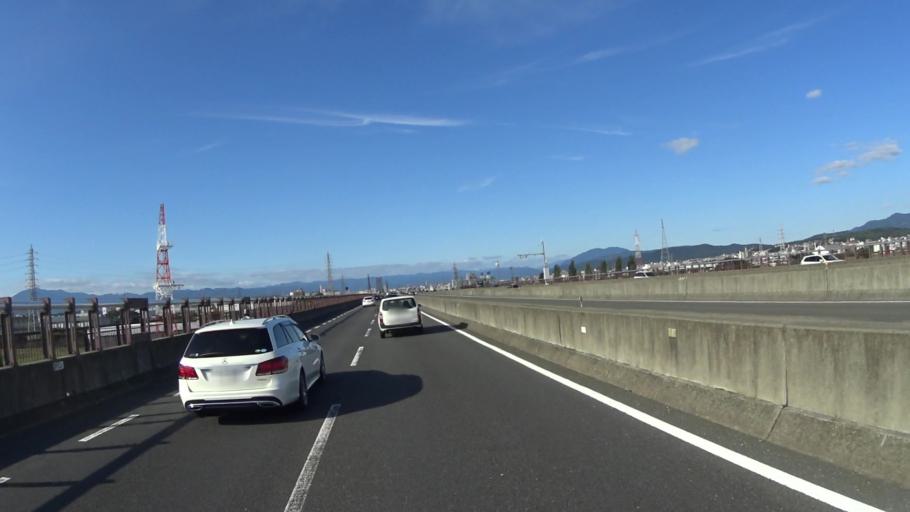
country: JP
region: Kyoto
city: Uji
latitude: 34.9192
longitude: 135.7504
